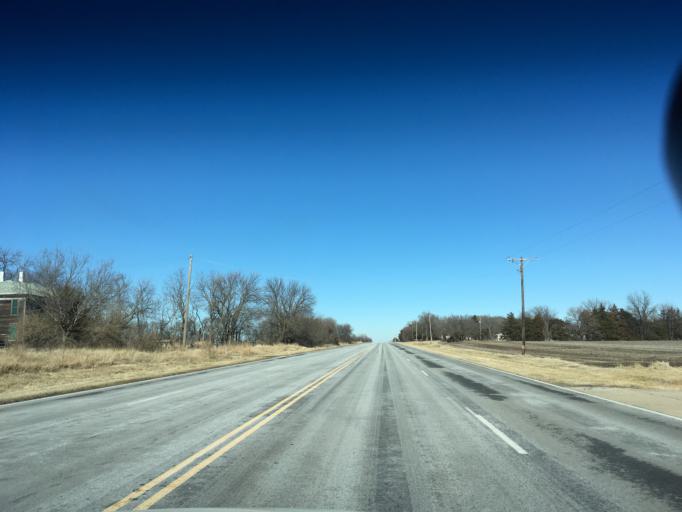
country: US
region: Kansas
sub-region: Harvey County
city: Sedgwick
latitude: 37.9202
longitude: -97.3365
